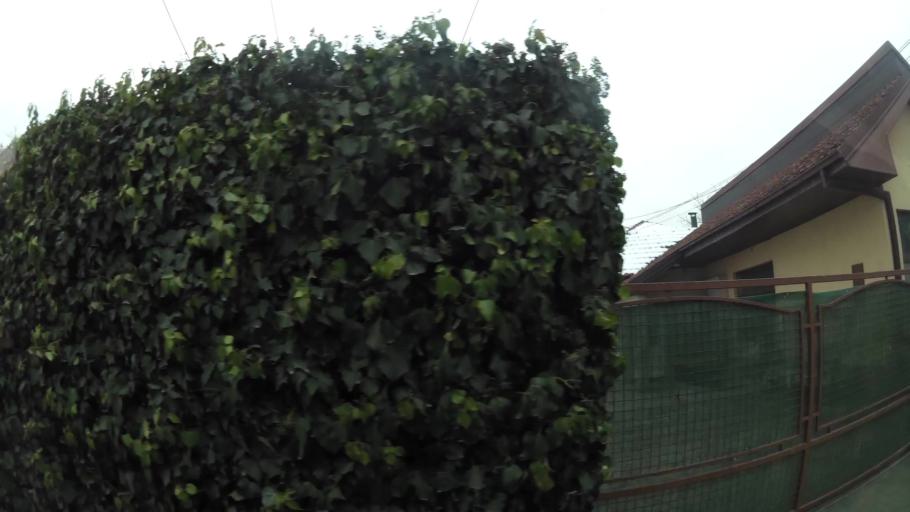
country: MK
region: Saraj
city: Saraj
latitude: 42.0413
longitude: 21.3510
